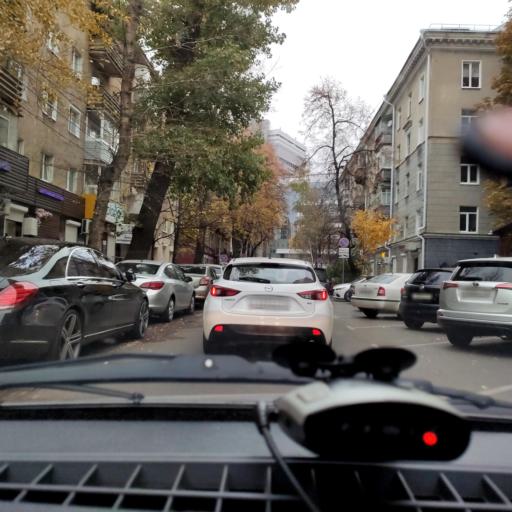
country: RU
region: Voronezj
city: Voronezh
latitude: 51.6589
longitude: 39.1968
